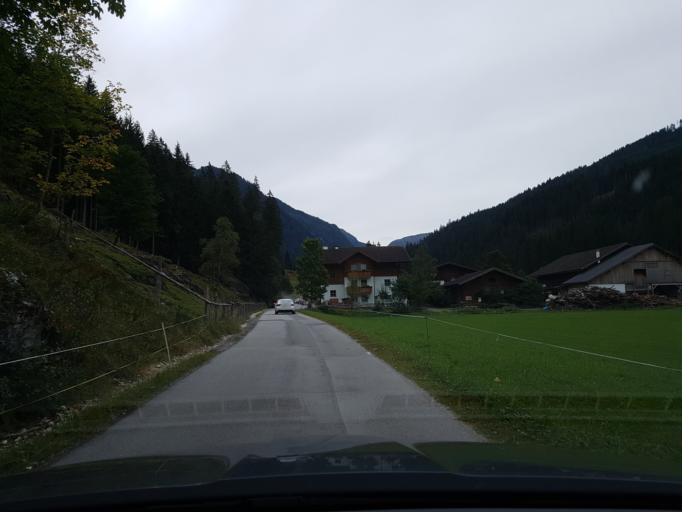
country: AT
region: Salzburg
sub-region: Politischer Bezirk Sankt Johann im Pongau
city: Forstau
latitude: 47.3530
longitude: 13.5719
